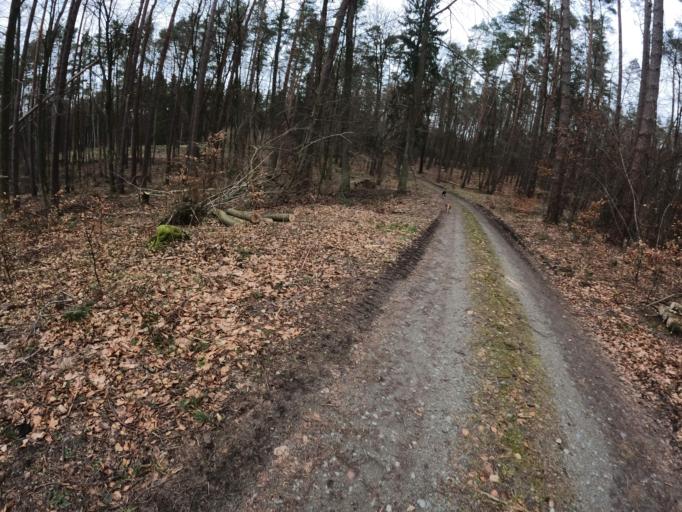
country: PL
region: West Pomeranian Voivodeship
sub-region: Powiat kamienski
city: Golczewo
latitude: 53.8152
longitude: 15.0258
